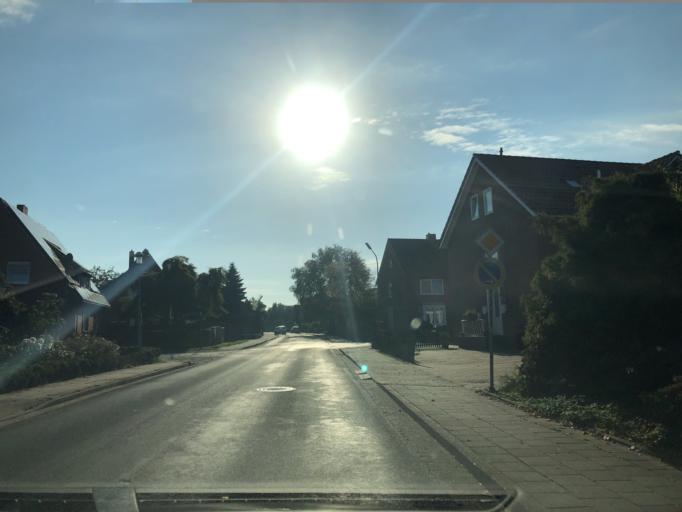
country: DE
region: Lower Saxony
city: Papenburg
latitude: 53.0823
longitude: 7.4058
